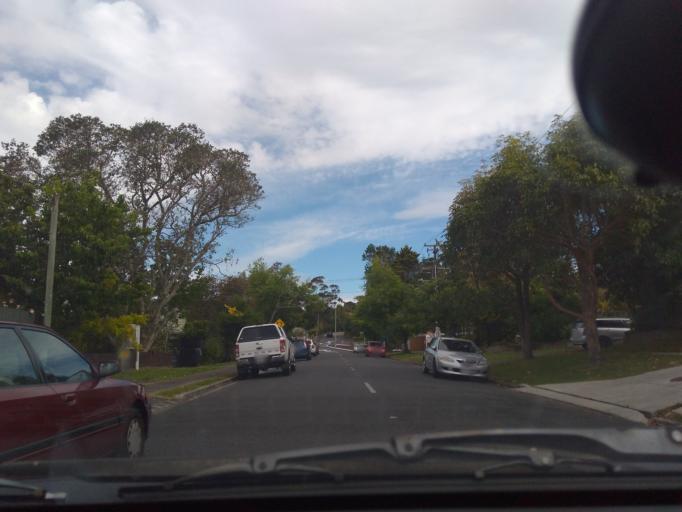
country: NZ
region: Auckland
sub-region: Auckland
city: Waitakere
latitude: -36.9214
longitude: 174.6702
